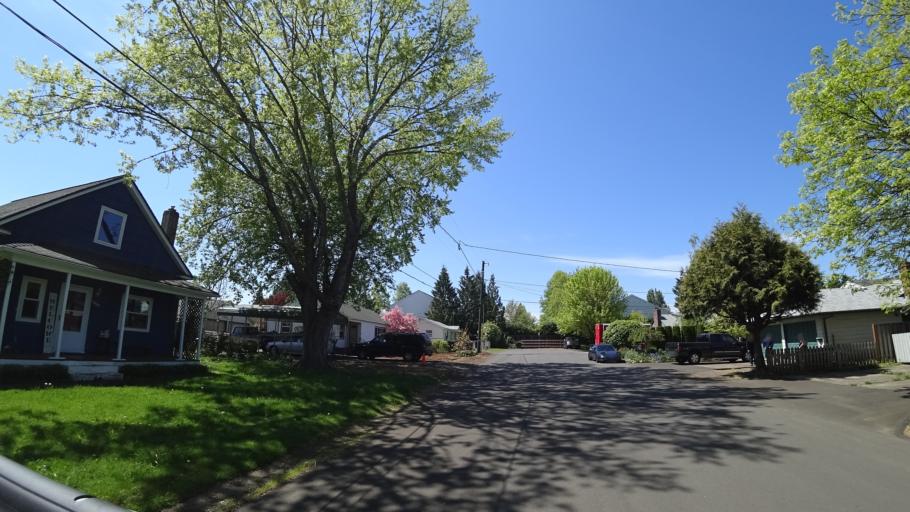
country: US
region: Oregon
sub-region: Washington County
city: Hillsboro
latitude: 45.5153
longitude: -122.9651
